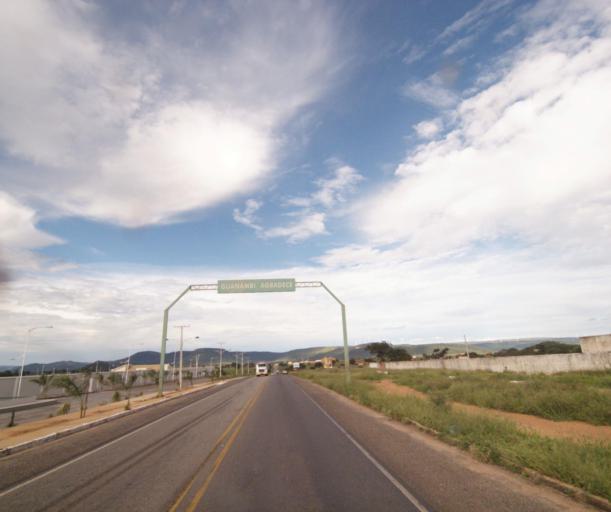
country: BR
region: Bahia
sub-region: Guanambi
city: Guanambi
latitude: -14.1986
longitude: -42.7527
